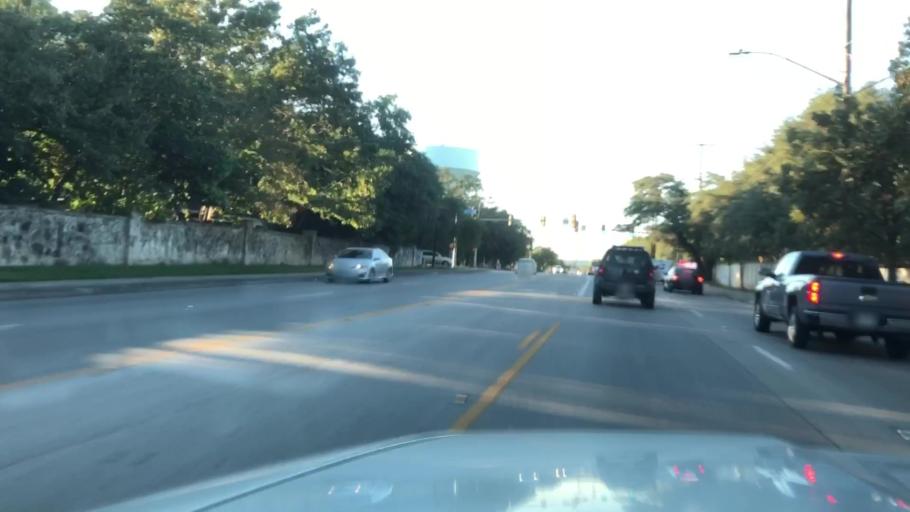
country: US
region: Texas
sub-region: Bexar County
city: Leon Valley
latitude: 29.5400
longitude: -98.6109
